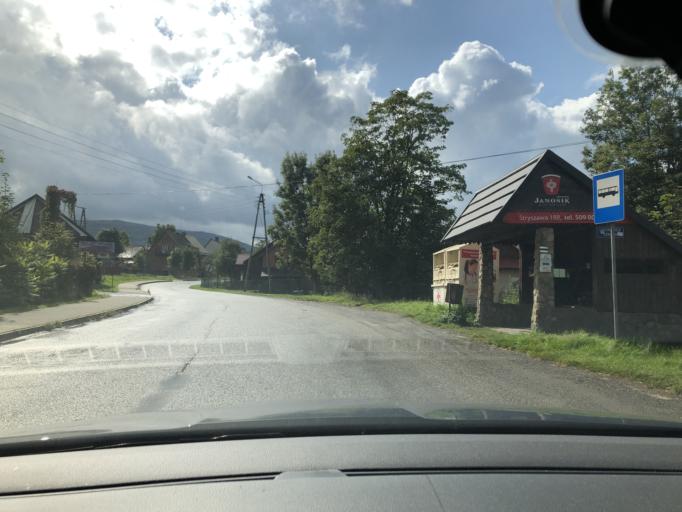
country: PL
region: Lesser Poland Voivodeship
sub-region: Powiat suski
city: Lachowice
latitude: 49.7123
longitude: 19.4701
